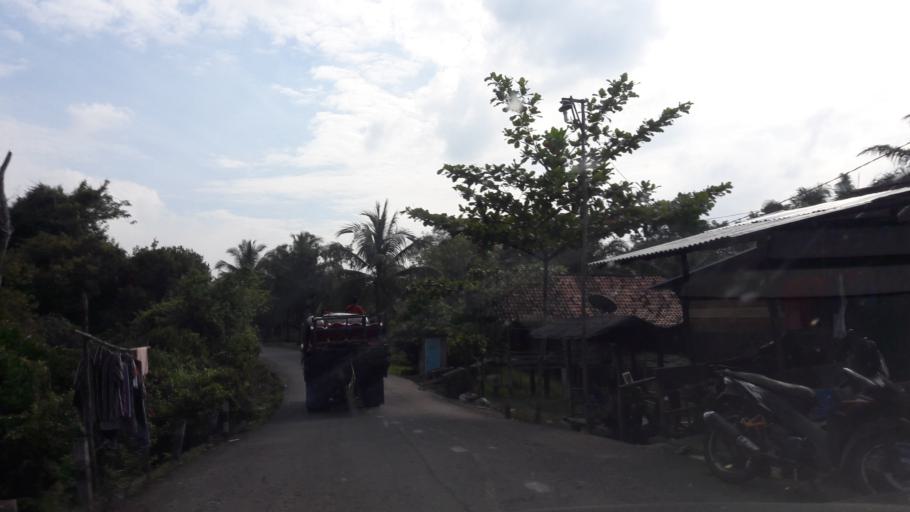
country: ID
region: South Sumatra
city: Gunungmenang
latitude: -3.1081
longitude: 103.9569
